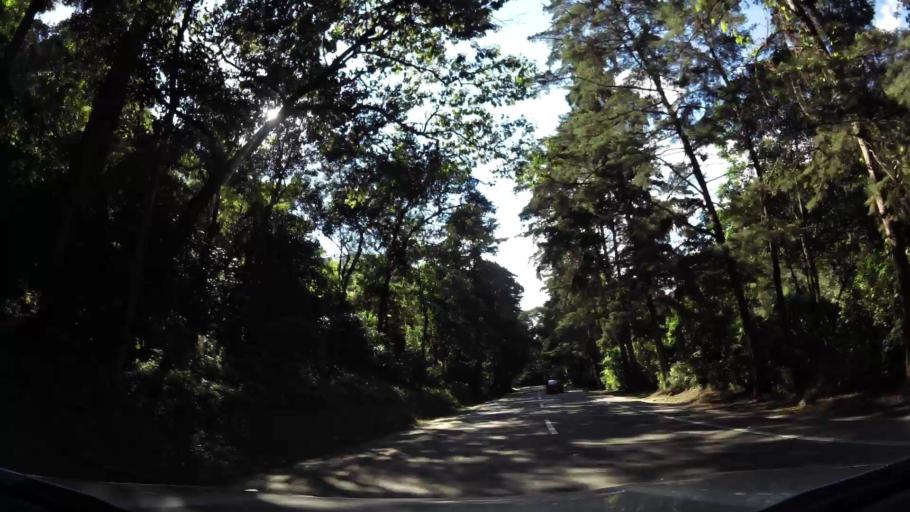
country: GT
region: Sacatepequez
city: Antigua Guatemala
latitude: 14.5595
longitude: -90.7059
